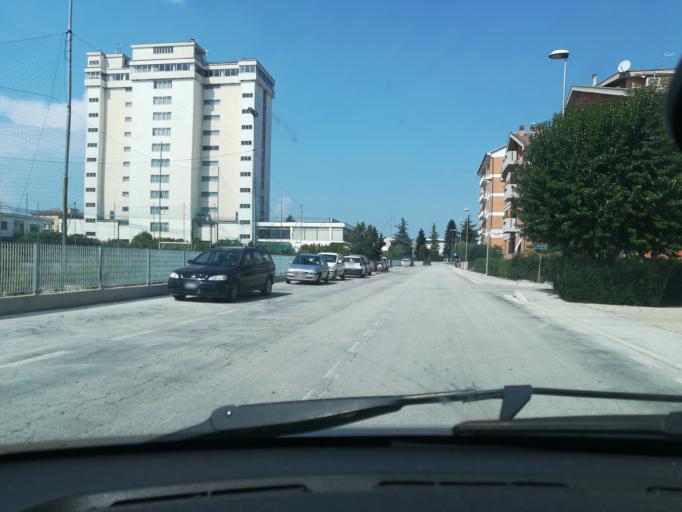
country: IT
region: The Marches
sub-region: Provincia di Macerata
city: Casette Verdini
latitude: 43.2514
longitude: 13.4080
